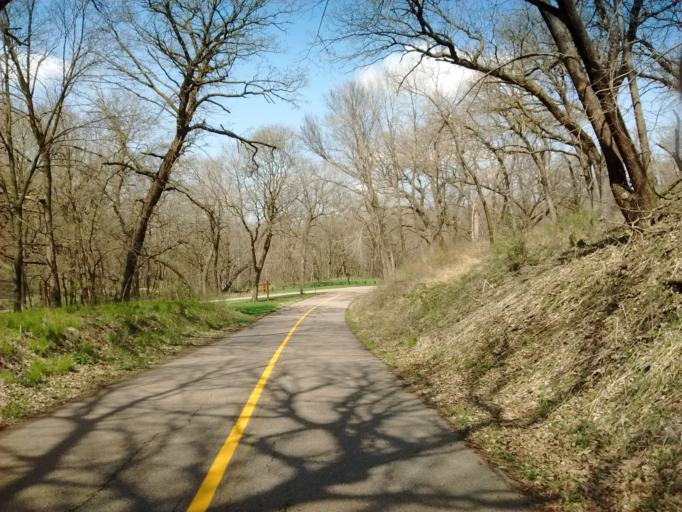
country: US
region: South Dakota
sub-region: Union County
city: North Sioux City
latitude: 42.5568
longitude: -96.4667
